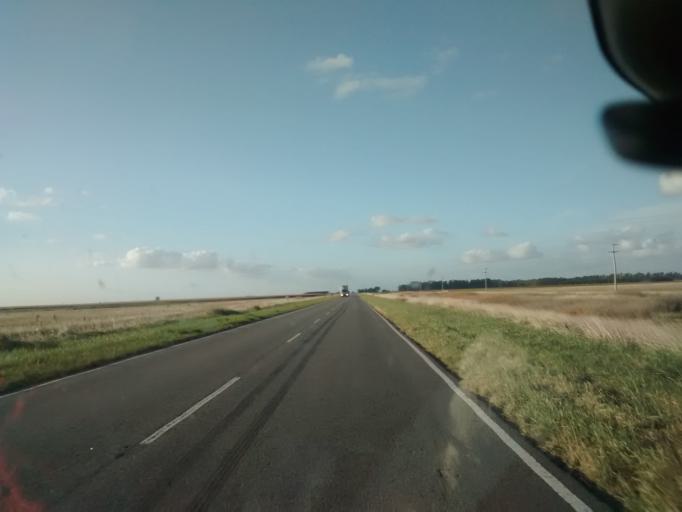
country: AR
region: Buenos Aires
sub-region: Partido de General Belgrano
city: General Belgrano
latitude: -36.0549
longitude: -58.6252
